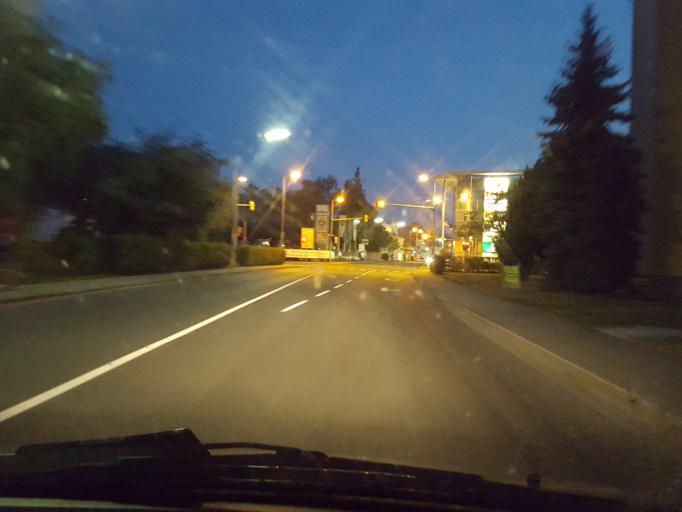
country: AT
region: Lower Austria
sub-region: Politischer Bezirk Scheibbs
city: Wieselburg
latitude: 48.1332
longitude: 15.1408
